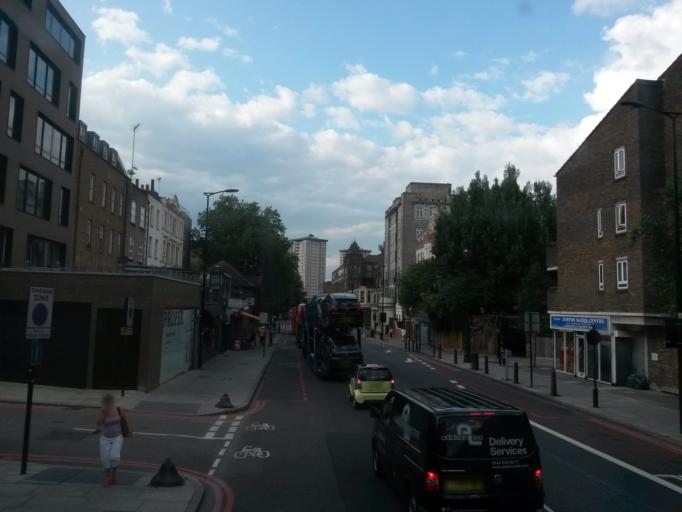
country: GB
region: England
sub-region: Greater London
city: Camden Town
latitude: 51.5276
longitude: -0.1386
